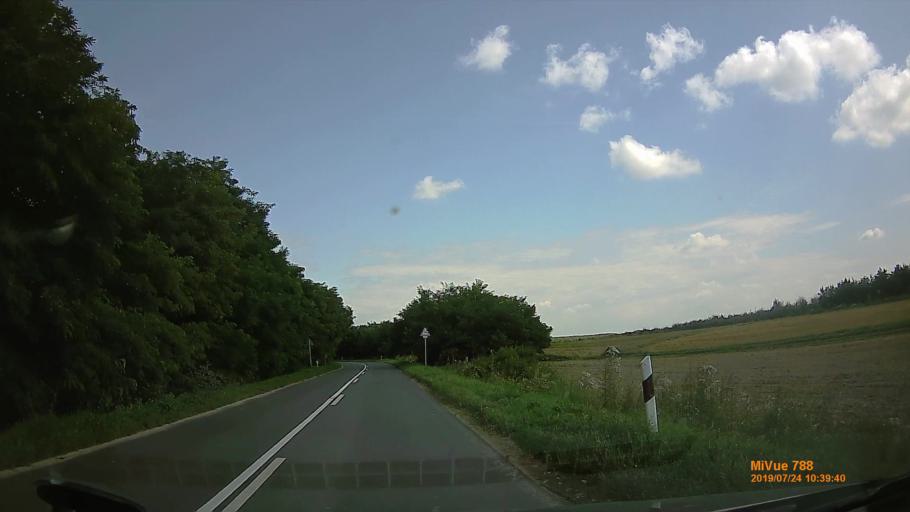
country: HU
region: Szabolcs-Szatmar-Bereg
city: Tarpa
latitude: 48.1666
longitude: 22.5429
